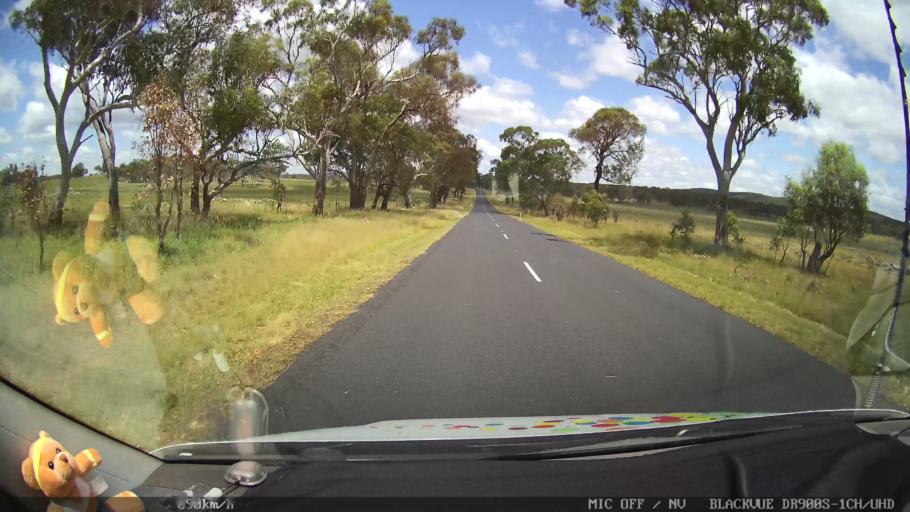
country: AU
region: New South Wales
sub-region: Glen Innes Severn
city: Glen Innes
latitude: -29.4694
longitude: 151.6535
